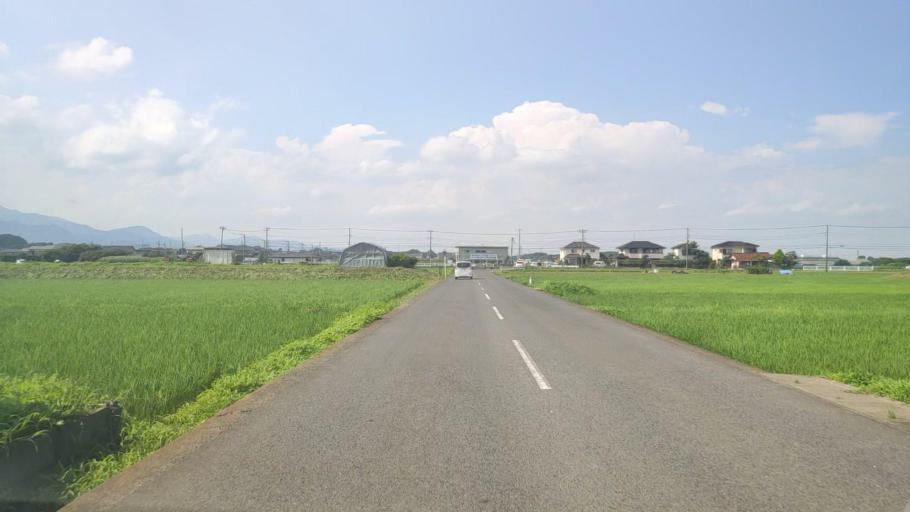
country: JP
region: Kanagawa
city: Isehara
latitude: 35.3617
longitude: 139.3163
